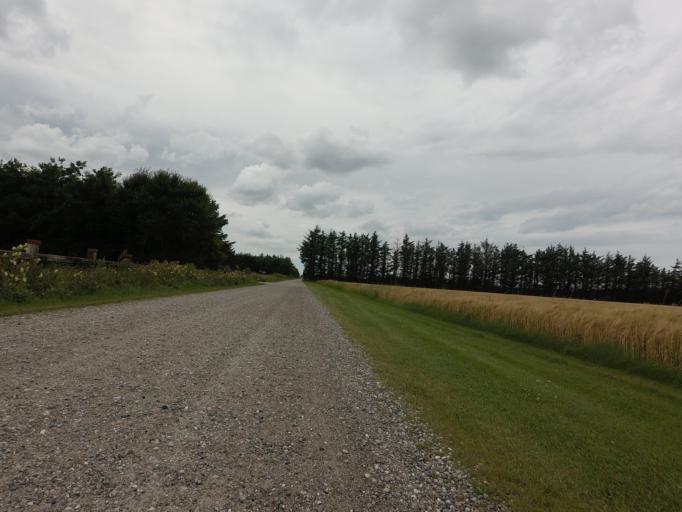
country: DK
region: North Denmark
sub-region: Jammerbugt Kommune
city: Pandrup
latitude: 57.3386
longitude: 9.7062
